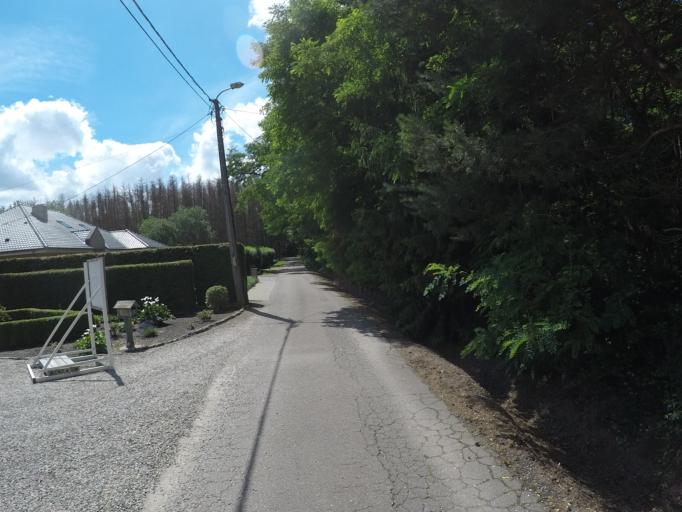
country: BE
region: Flanders
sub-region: Provincie Antwerpen
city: Vosselaar
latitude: 51.3282
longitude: 4.8878
